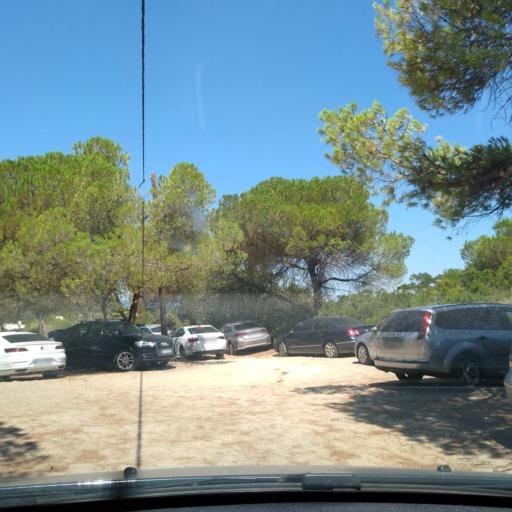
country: GR
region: Central Macedonia
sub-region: Nomos Chalkidikis
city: Neos Marmaras
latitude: 40.1934
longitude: 23.8069
